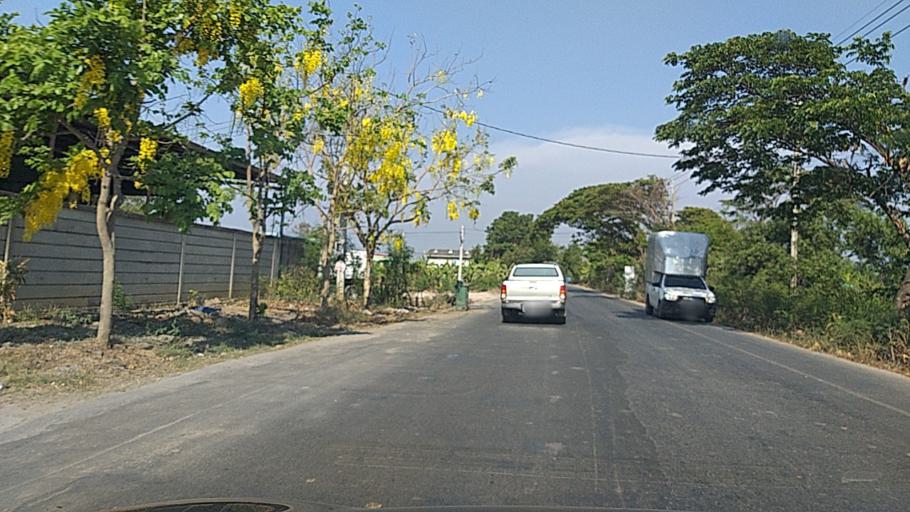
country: TH
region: Nonthaburi
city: Bang Yai
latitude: 13.8820
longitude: 100.3245
